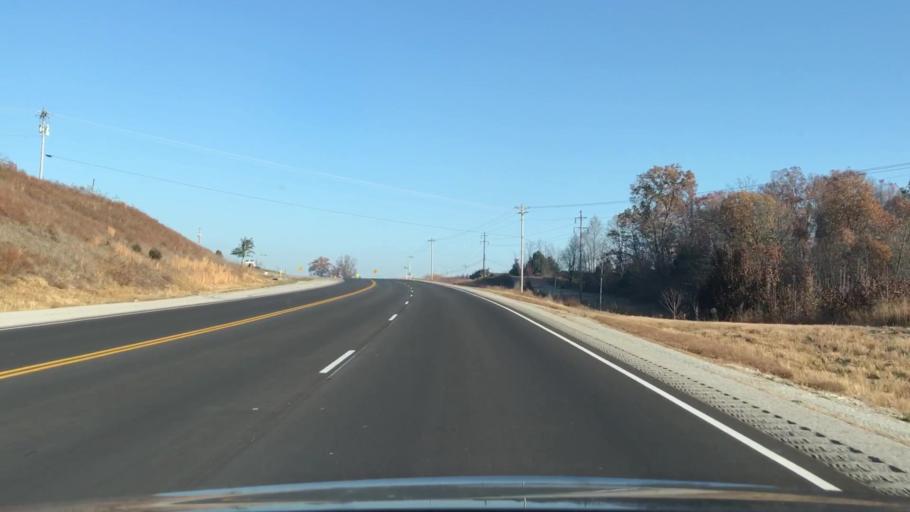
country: US
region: Kentucky
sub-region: Edmonson County
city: Brownsville
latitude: 37.1005
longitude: -86.2300
